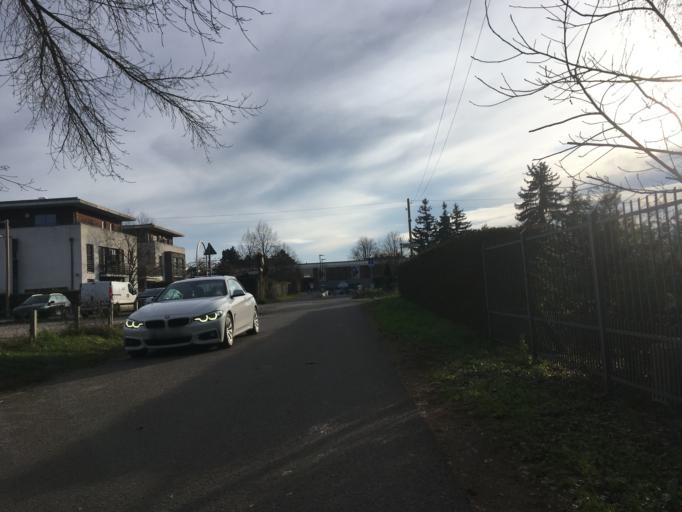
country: DE
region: Berlin
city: Biesdorf
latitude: 52.5011
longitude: 13.5468
